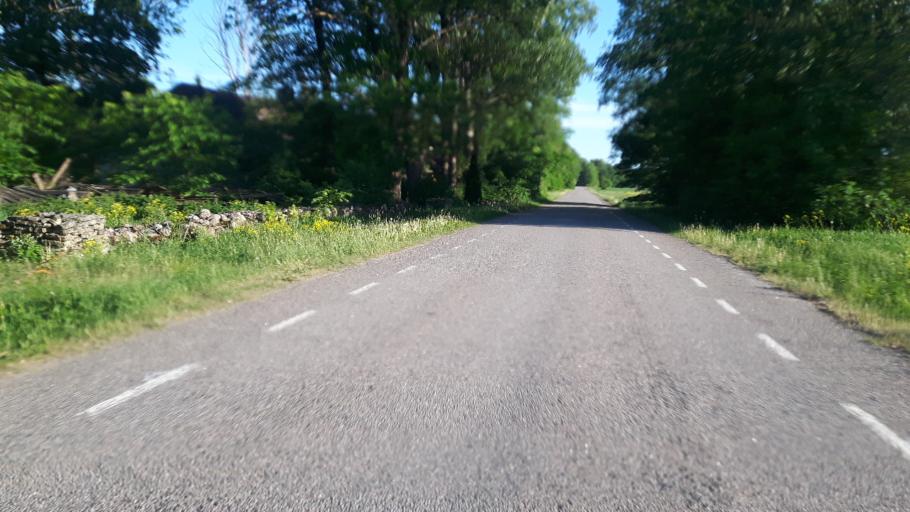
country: EE
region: Raplamaa
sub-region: Kehtna vald
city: Kehtna
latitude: 58.8962
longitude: 24.8799
